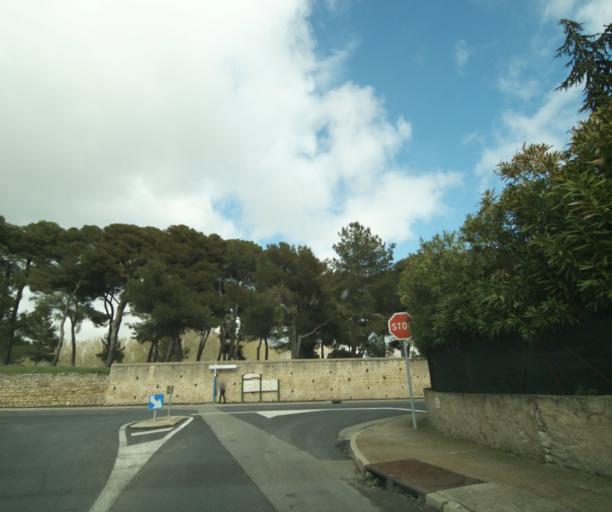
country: FR
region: Languedoc-Roussillon
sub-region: Departement de l'Herault
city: Pignan
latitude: 43.5798
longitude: 3.7593
